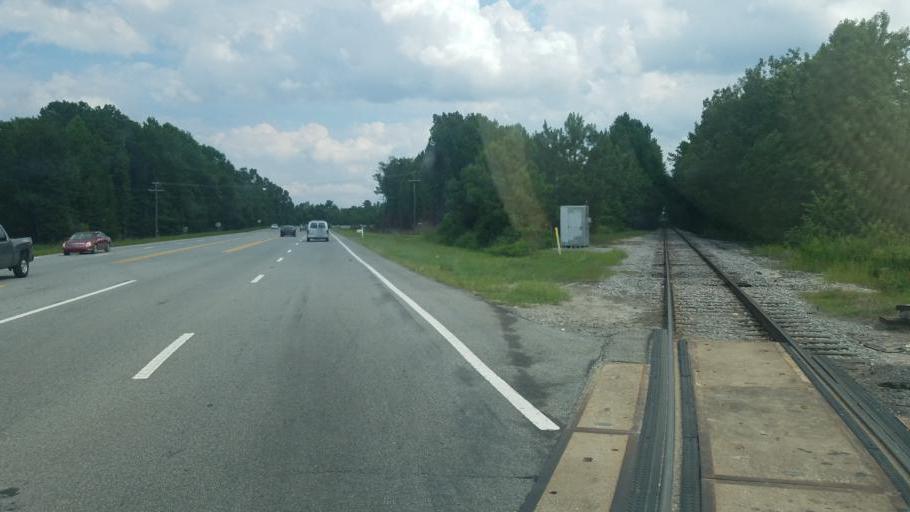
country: US
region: North Carolina
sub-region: Currituck County
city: Moyock
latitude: 36.4988
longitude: -76.1428
